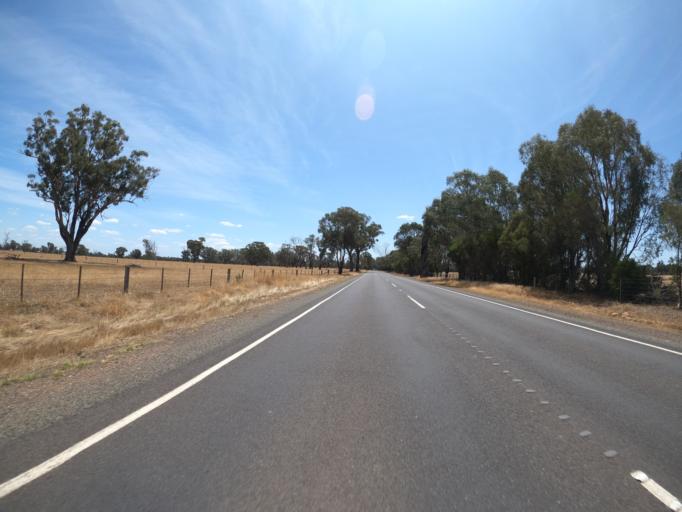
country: AU
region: Victoria
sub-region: Benalla
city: Benalla
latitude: -36.5081
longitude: 146.0268
